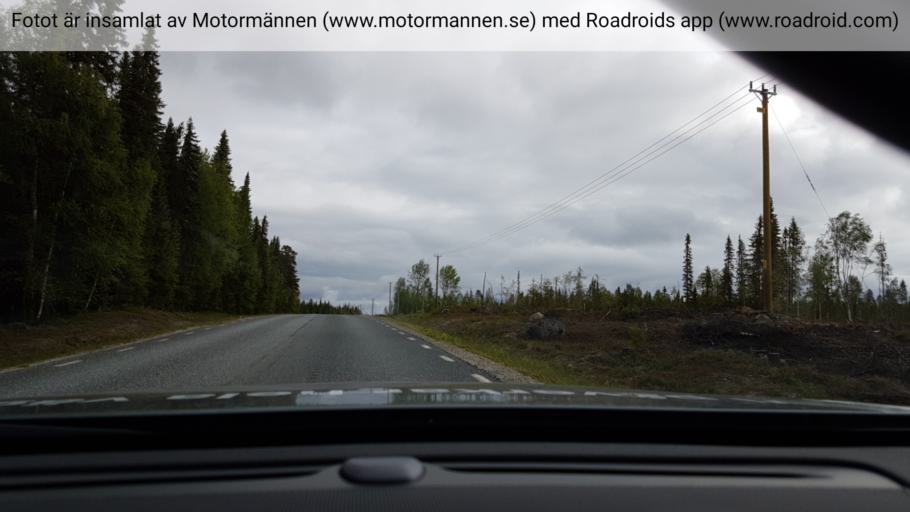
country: SE
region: Vaesterbotten
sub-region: Asele Kommun
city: Insjon
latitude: 64.2806
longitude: 17.6096
